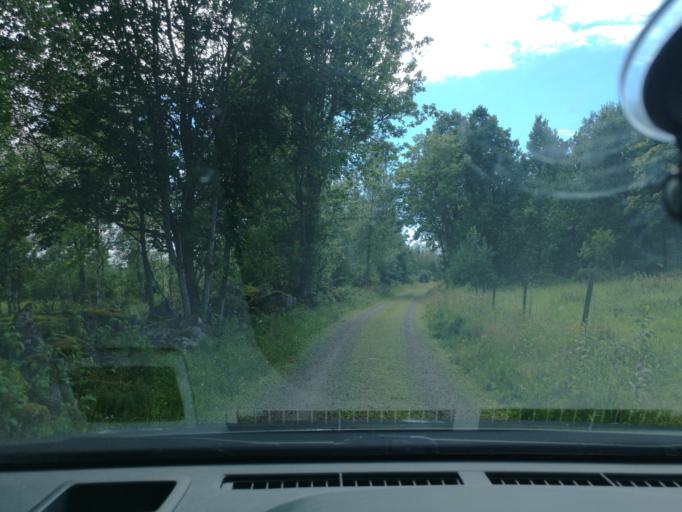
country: SE
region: Kronoberg
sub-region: Alvesta Kommun
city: Vislanda
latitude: 56.6992
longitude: 14.4105
